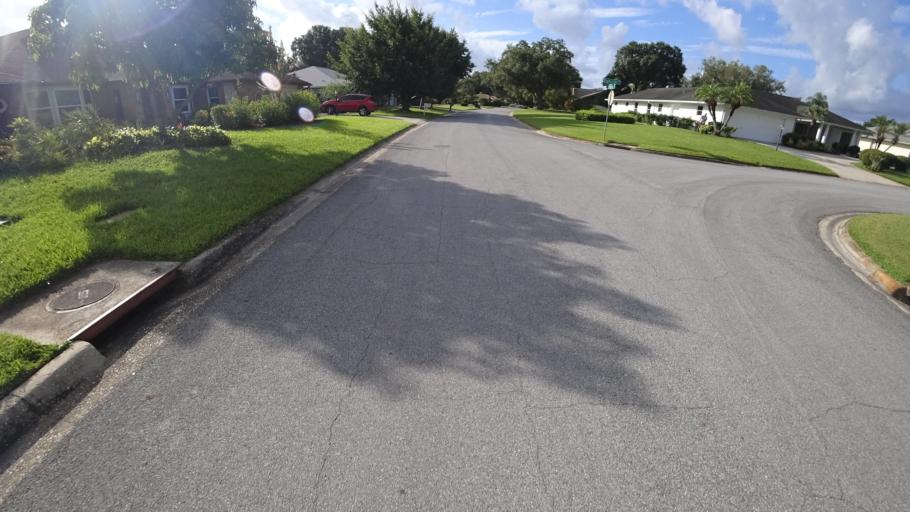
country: US
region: Florida
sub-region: Sarasota County
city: Desoto Lakes
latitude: 27.4199
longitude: -82.4909
